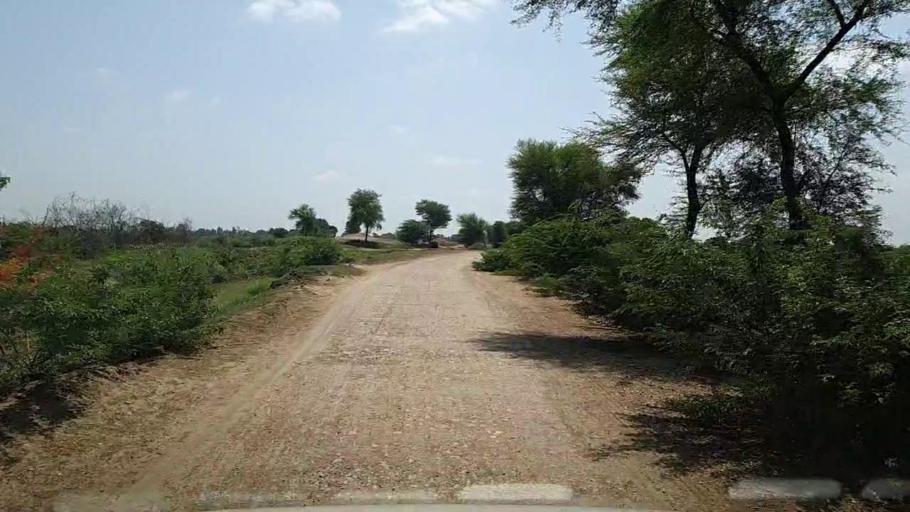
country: PK
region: Sindh
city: Kario
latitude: 24.8661
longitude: 68.6873
